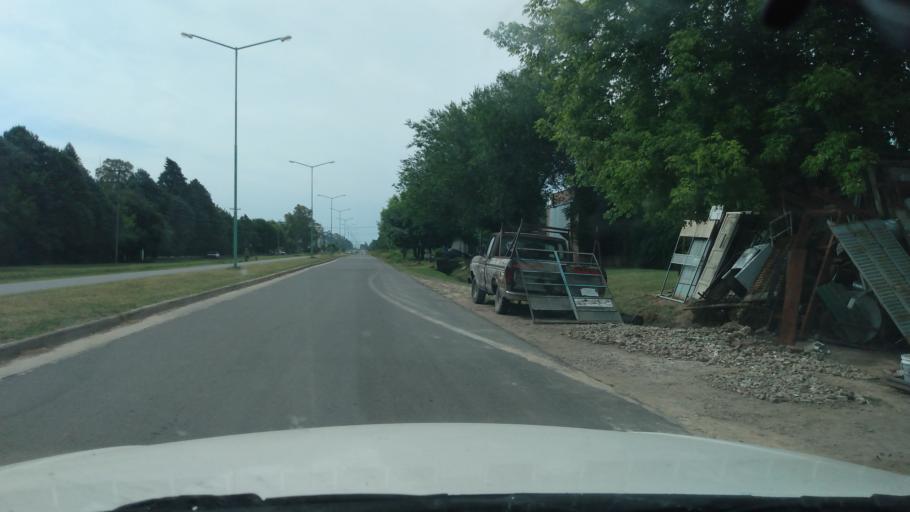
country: AR
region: Buenos Aires
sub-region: Partido de Lujan
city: Lujan
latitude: -34.5575
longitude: -59.1301
